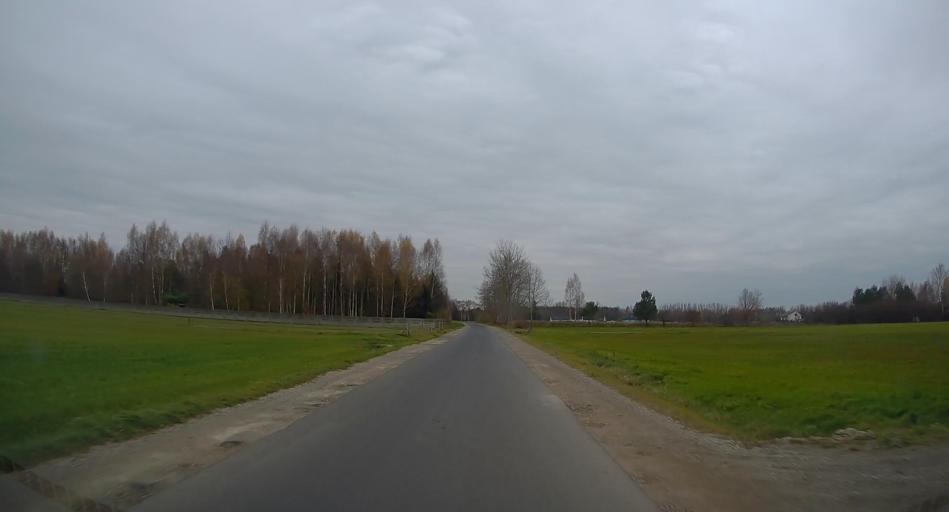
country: PL
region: Lodz Voivodeship
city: Zabia Wola
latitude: 51.9924
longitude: 20.6600
